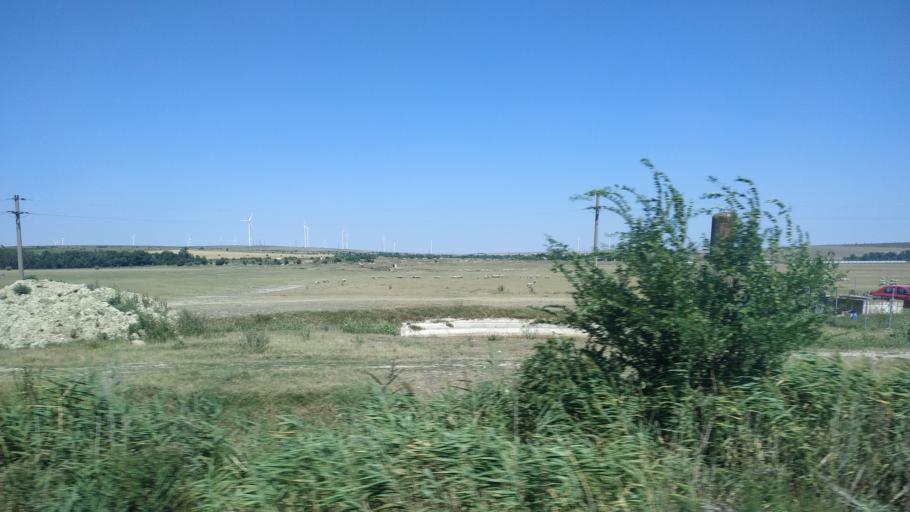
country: RO
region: Constanta
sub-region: Comuna Mircea Voda
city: Mircea Voda
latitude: 44.2640
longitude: 28.1676
